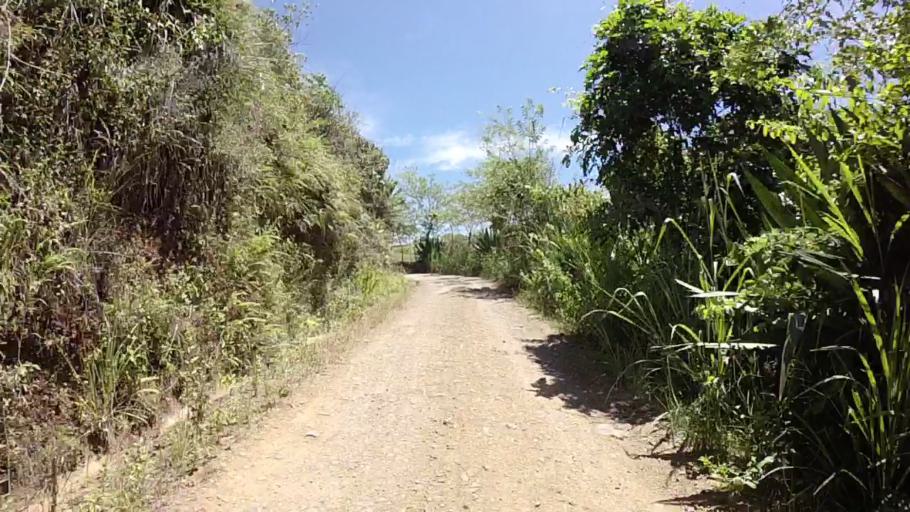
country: CO
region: Valle del Cauca
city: Alcala
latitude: 4.7031
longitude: -75.8275
